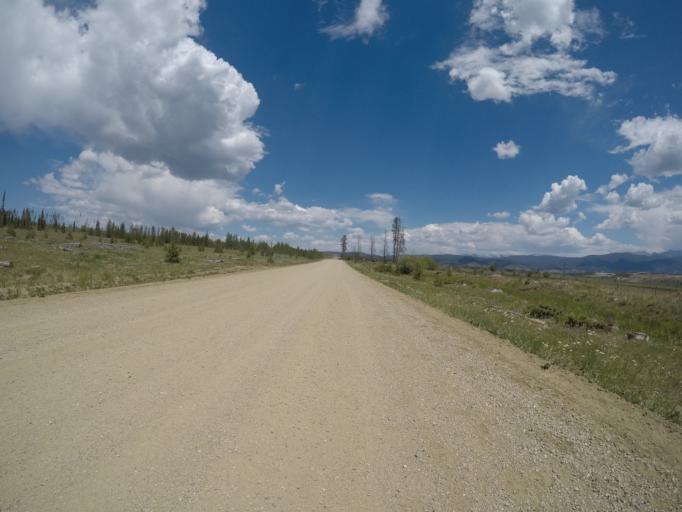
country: US
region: Colorado
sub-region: Grand County
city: Fraser
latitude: 39.9525
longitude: -105.8688
